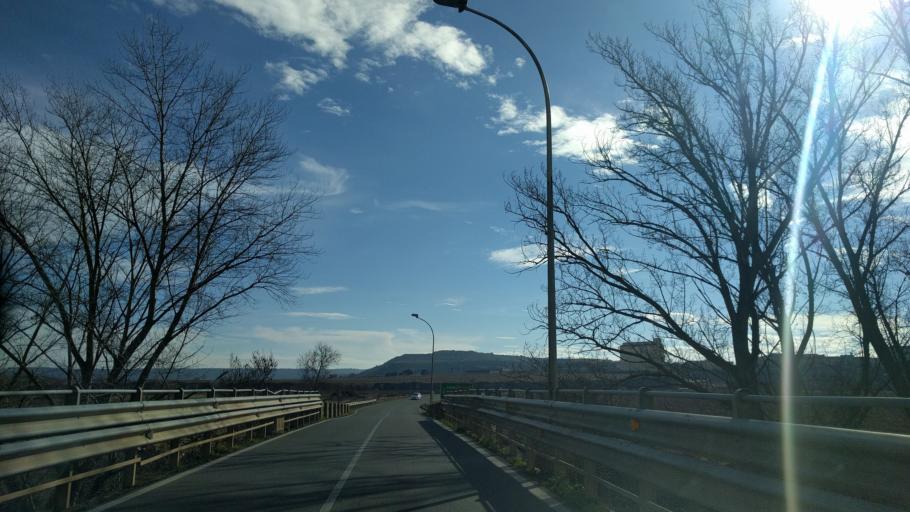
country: ES
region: Basque Country
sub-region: Provincia de Alava
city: Lapuebla de Labarca
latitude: 42.4924
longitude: -2.5730
